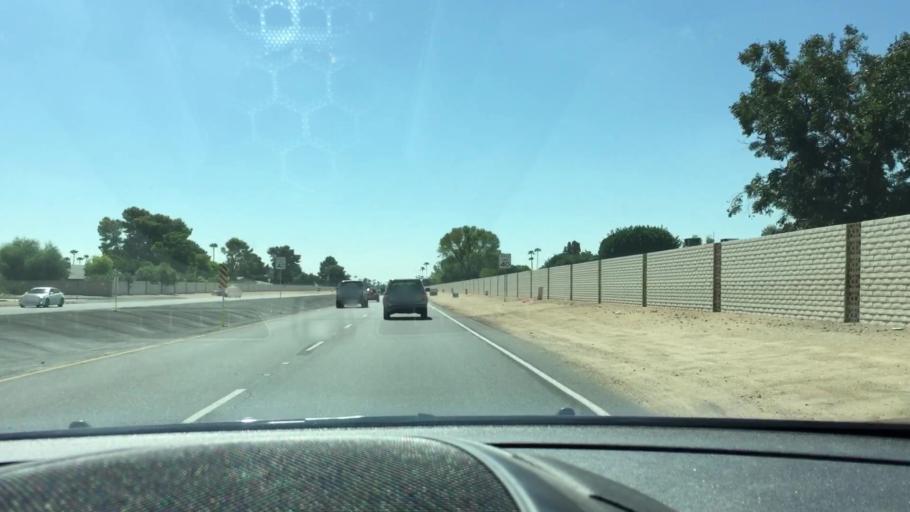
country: US
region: Arizona
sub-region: Maricopa County
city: Sun City
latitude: 33.6513
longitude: -112.2786
